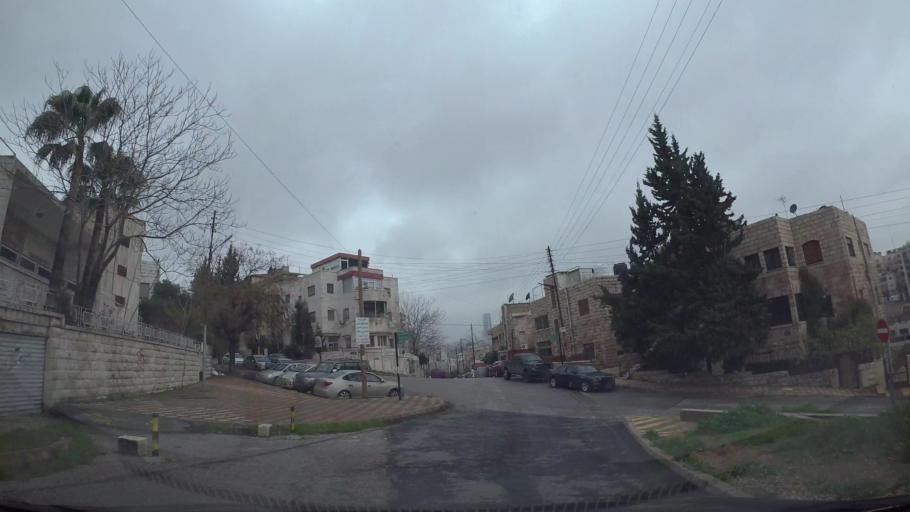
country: JO
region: Amman
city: Amman
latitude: 31.9528
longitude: 35.9192
